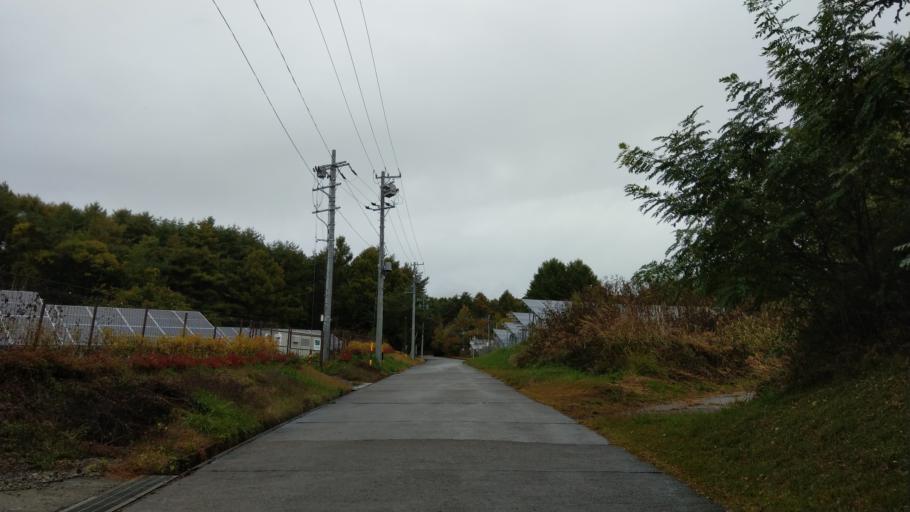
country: JP
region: Nagano
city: Komoro
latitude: 36.3639
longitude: 138.4263
